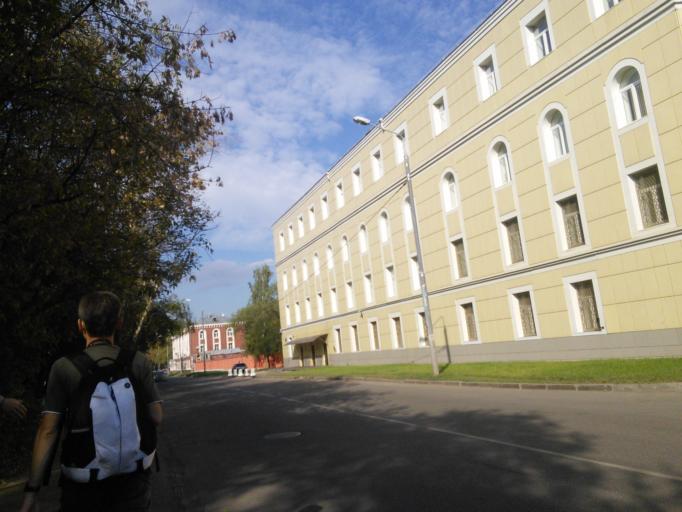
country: RU
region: Moscow
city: Mar'ina Roshcha
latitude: 55.8085
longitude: 37.5896
